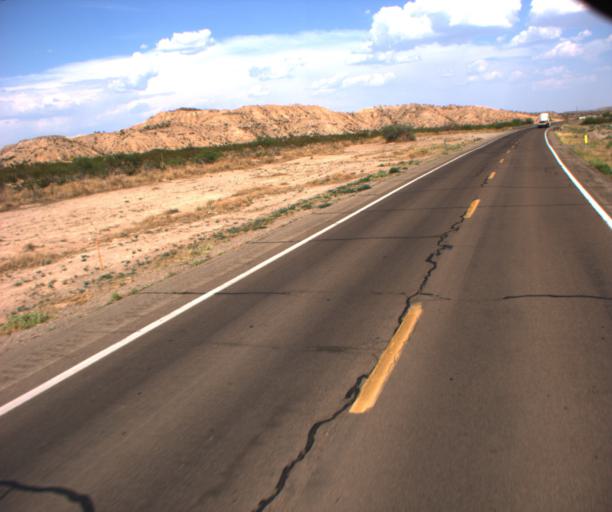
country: US
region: Arizona
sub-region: Greenlee County
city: Clifton
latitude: 32.7501
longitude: -109.1131
